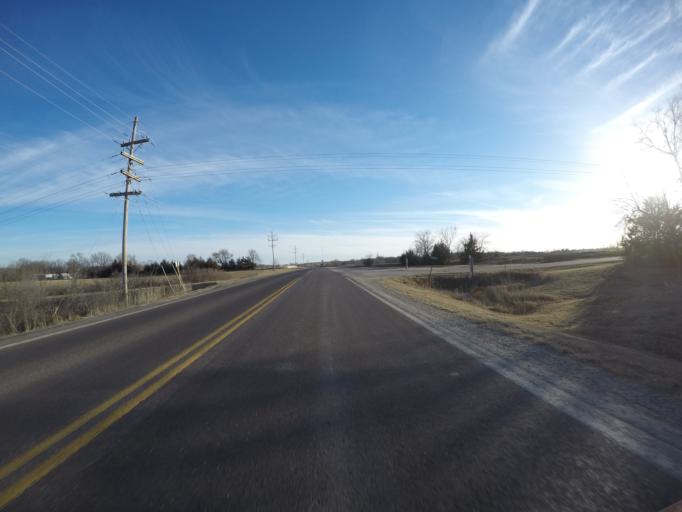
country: US
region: Kansas
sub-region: Marshall County
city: Marysville
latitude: 39.8497
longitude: -96.6667
